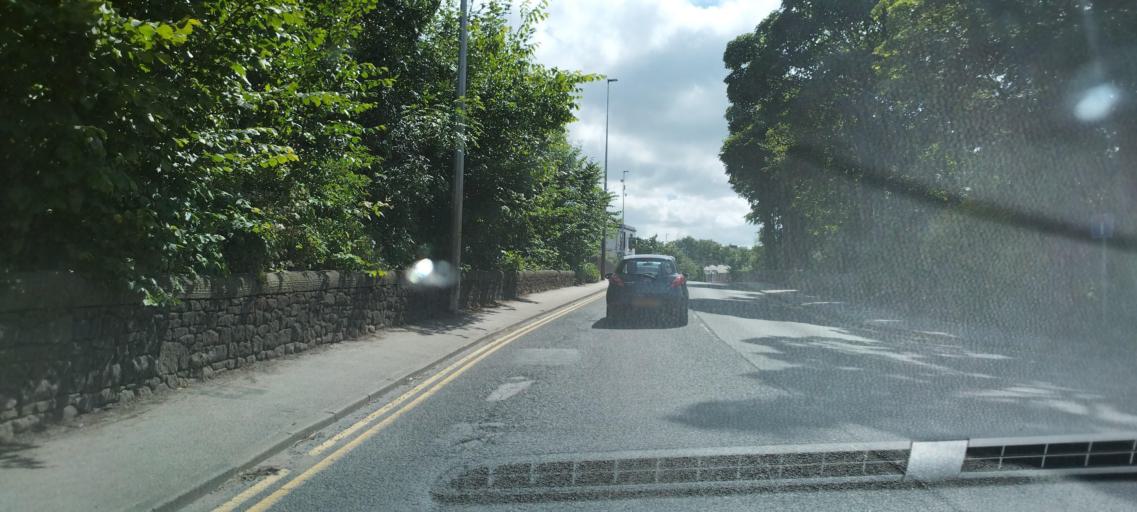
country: GB
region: England
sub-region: Blackburn with Darwen
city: Blackburn
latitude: 53.7335
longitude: -2.5193
